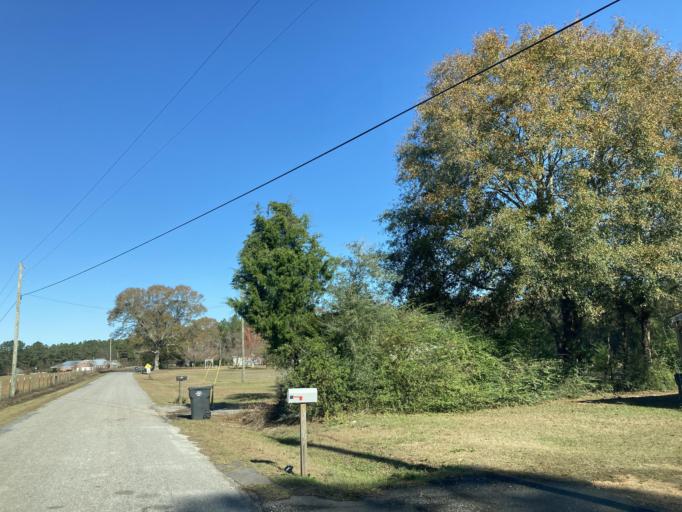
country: US
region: Mississippi
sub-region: Lamar County
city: Sumrall
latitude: 31.2678
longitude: -89.5308
